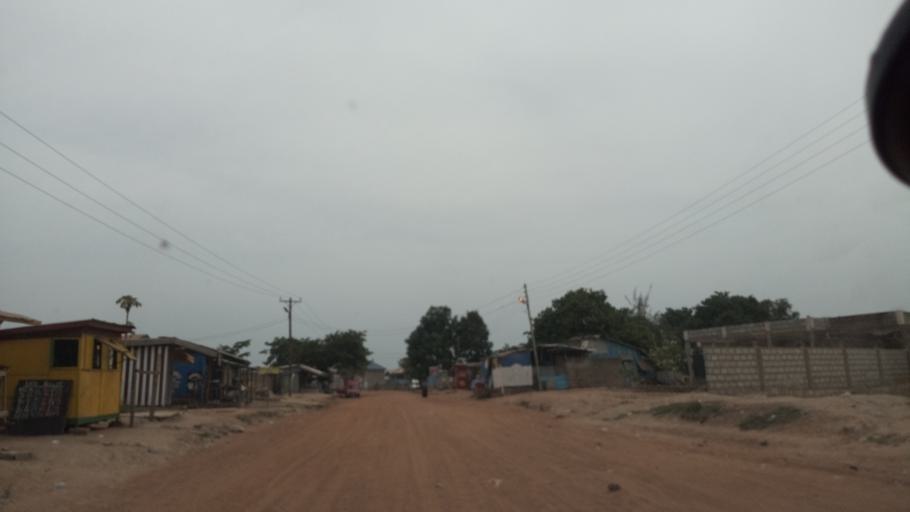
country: GH
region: Greater Accra
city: Medina Estates
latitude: 5.7042
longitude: -0.1344
